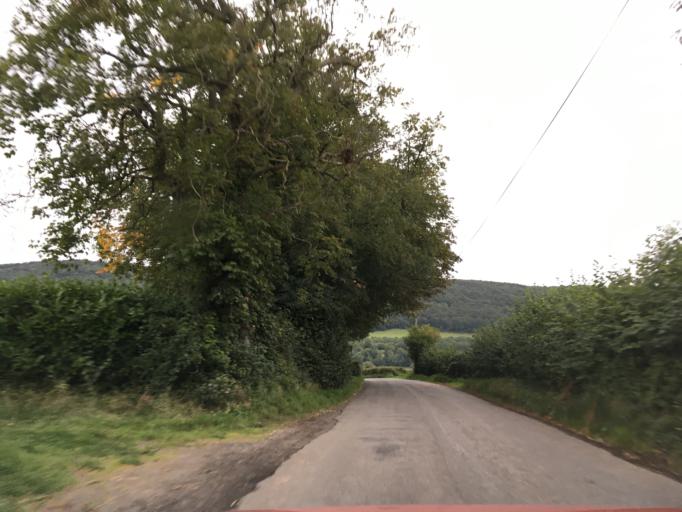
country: GB
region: Wales
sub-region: Monmouthshire
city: Llangybi
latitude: 51.6480
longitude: -2.8959
